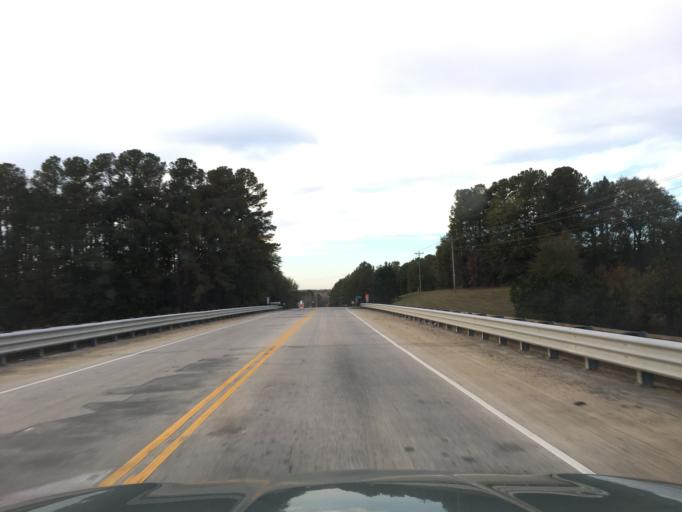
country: US
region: South Carolina
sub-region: Lexington County
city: Leesville
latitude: 33.8161
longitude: -81.4515
